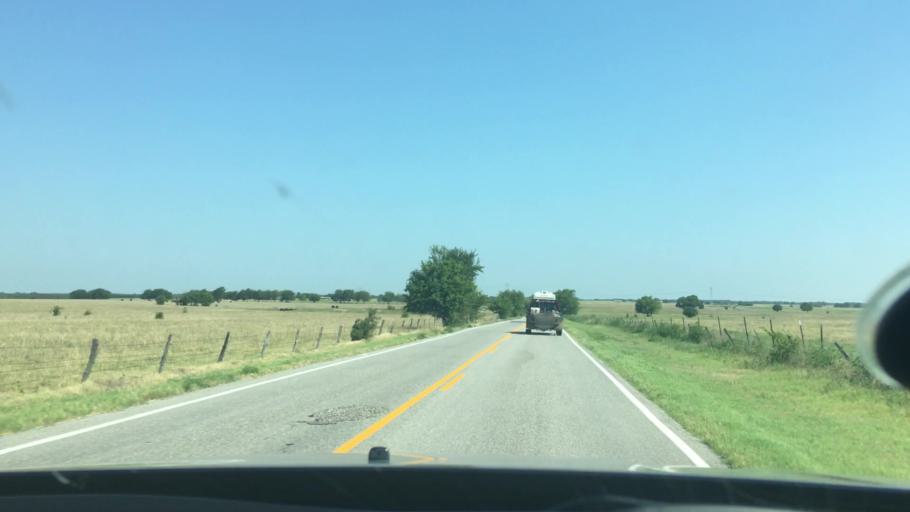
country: US
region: Oklahoma
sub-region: Johnston County
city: Tishomingo
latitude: 34.1514
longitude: -96.5057
